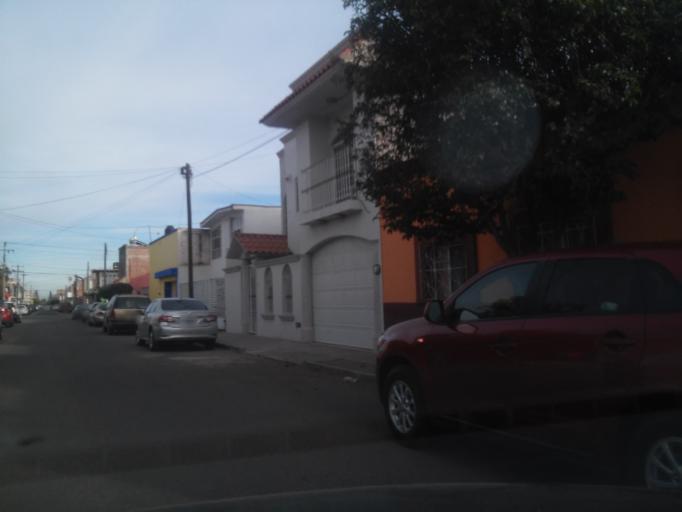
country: MX
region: Durango
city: Victoria de Durango
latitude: 24.0240
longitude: -104.6465
